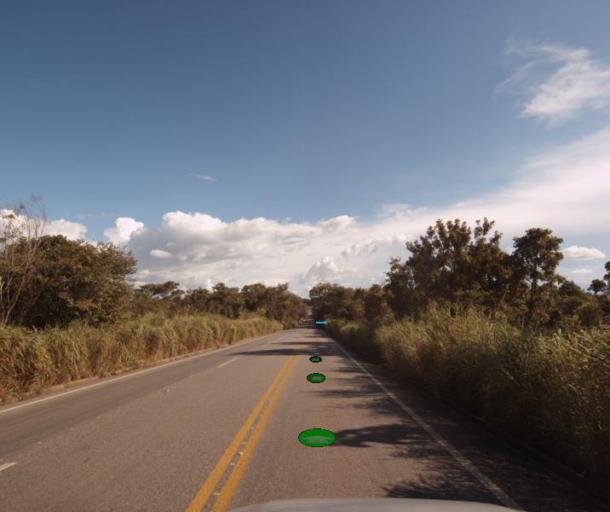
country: BR
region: Goias
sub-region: Porangatu
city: Porangatu
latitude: -13.0685
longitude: -49.1848
